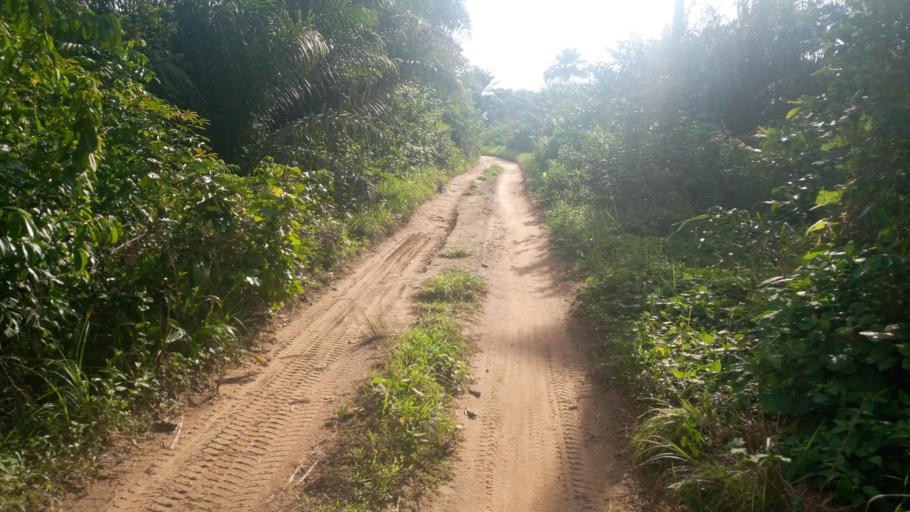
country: SL
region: Southern Province
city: Serabu
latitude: 7.6428
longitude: -12.1599
